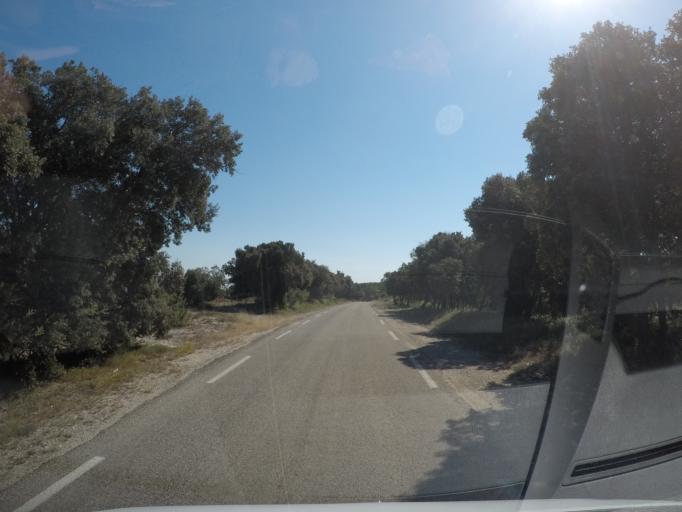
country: FR
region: Languedoc-Roussillon
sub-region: Departement du Gard
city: Tavel
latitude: 44.0141
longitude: 4.6522
